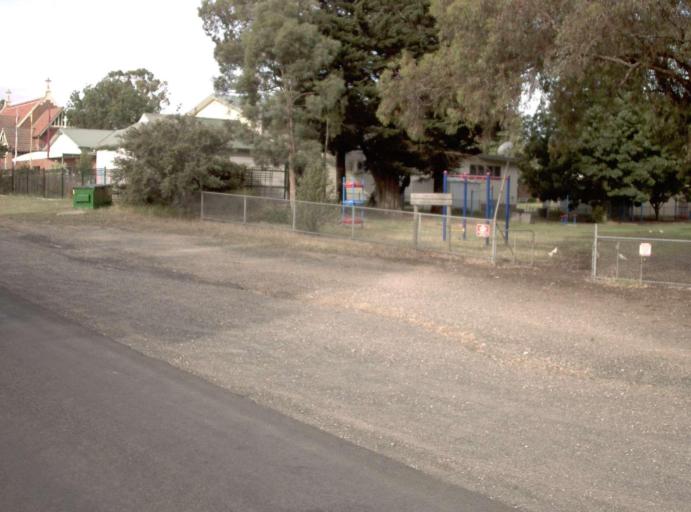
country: AU
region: Victoria
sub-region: Wellington
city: Heyfield
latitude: -37.9815
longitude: 146.7836
